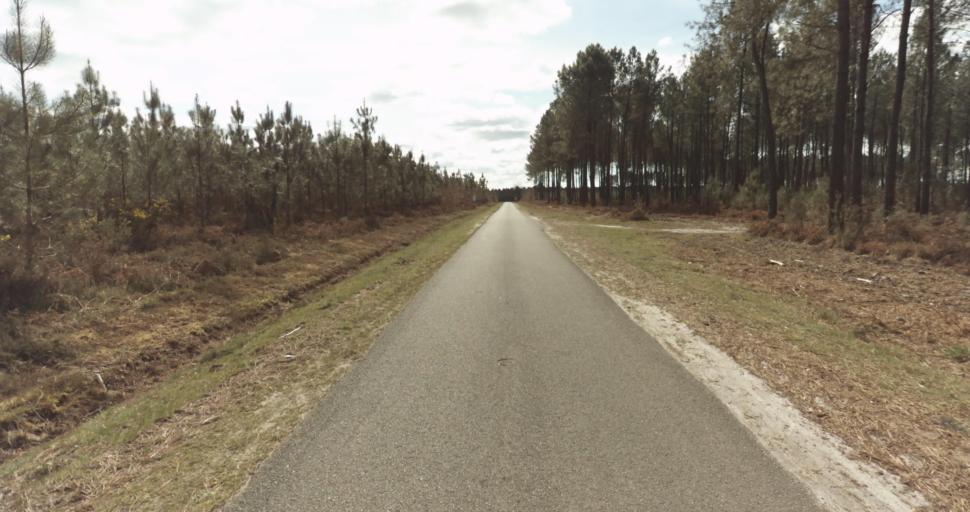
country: FR
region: Aquitaine
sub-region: Departement des Landes
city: Roquefort
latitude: 44.0370
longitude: -0.4231
